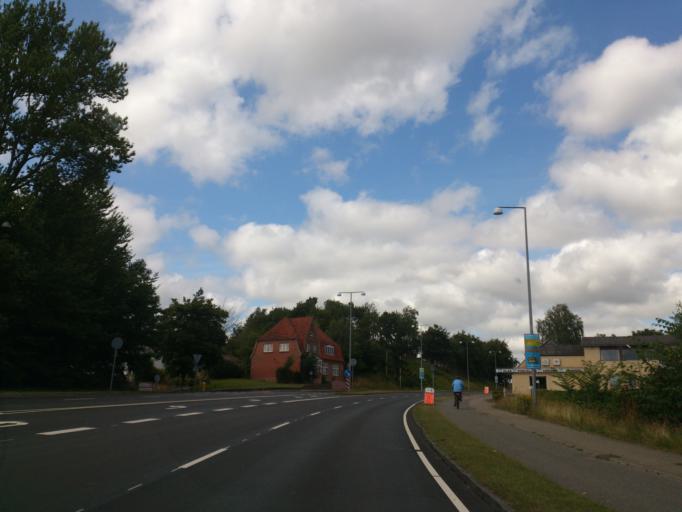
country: DK
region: South Denmark
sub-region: Aabenraa Kommune
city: Krusa
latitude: 54.8460
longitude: 9.4003
